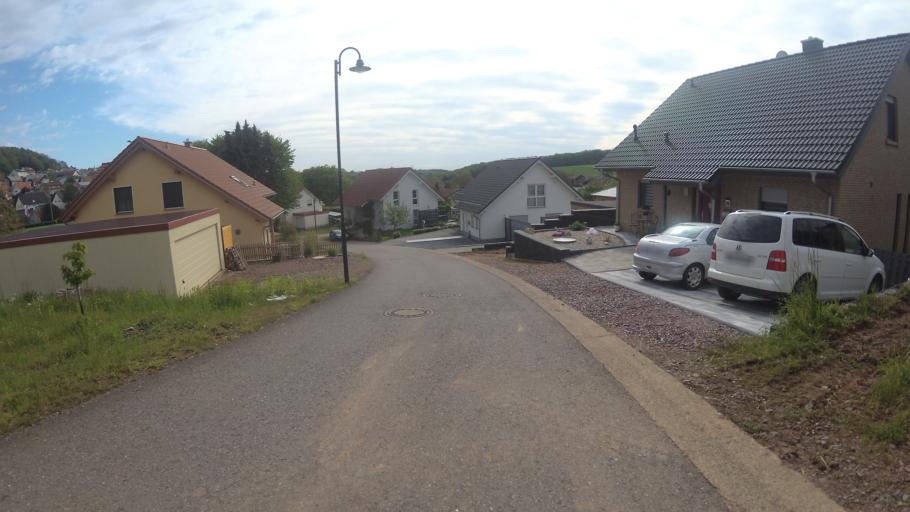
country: DE
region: Saarland
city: Orscholz
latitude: 49.4756
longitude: 6.5026
